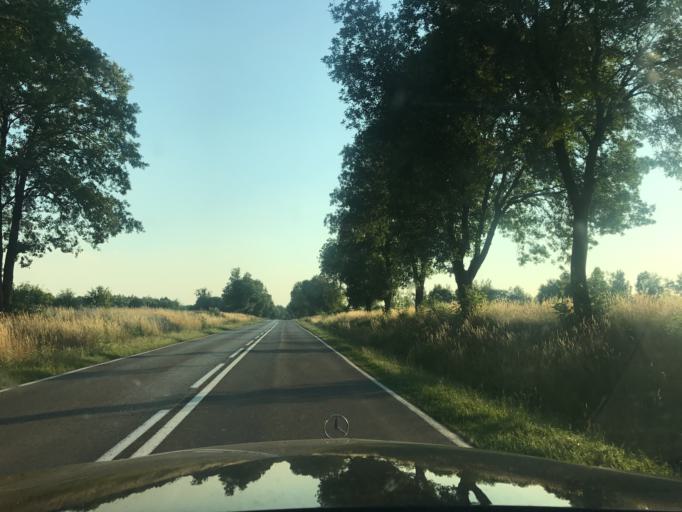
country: PL
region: Lublin Voivodeship
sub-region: Powiat parczewski
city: Debowa Kloda
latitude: 51.6483
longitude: 22.9820
